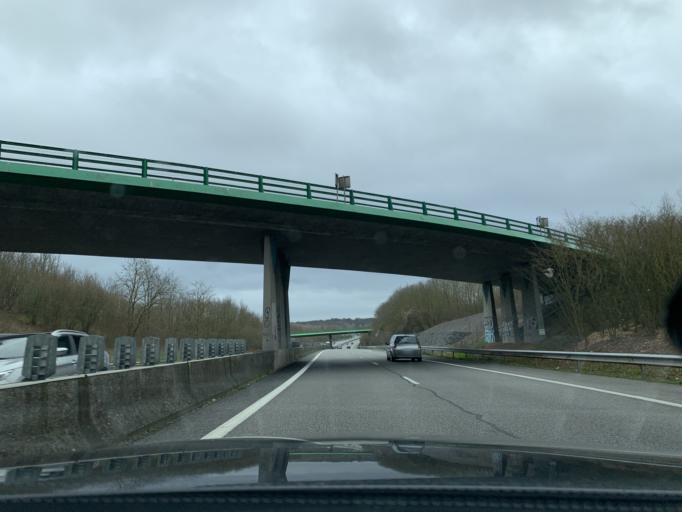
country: FR
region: Ile-de-France
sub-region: Departement du Val-d'Oise
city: Mours
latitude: 49.1287
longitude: 2.2534
